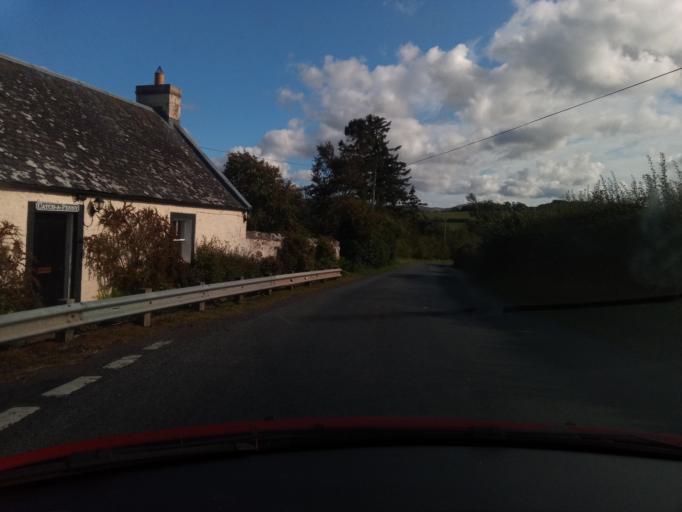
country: GB
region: Scotland
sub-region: The Scottish Borders
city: Coldstream
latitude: 55.5539
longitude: -2.3165
